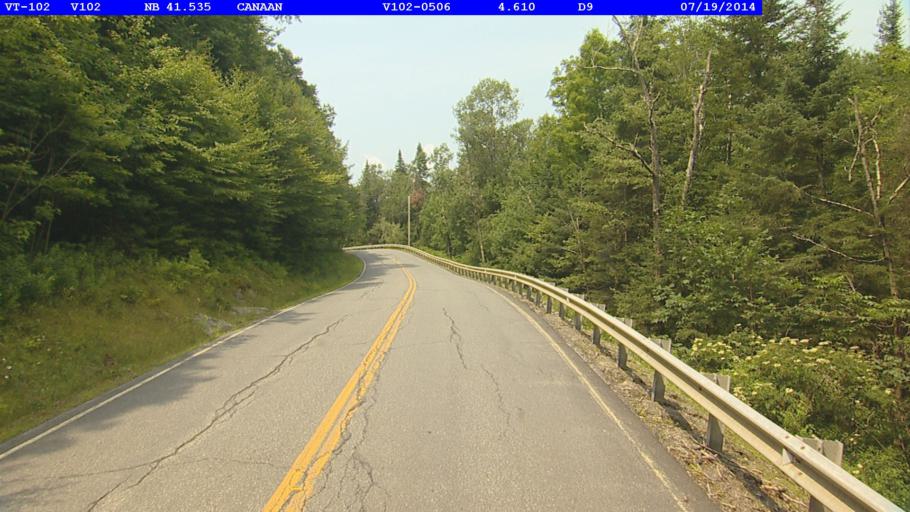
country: US
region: New Hampshire
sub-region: Coos County
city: Colebrook
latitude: 44.9706
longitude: -71.5273
